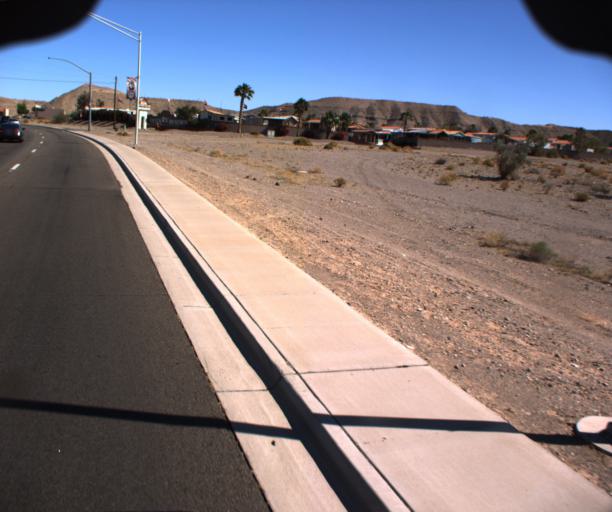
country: US
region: Arizona
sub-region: Mohave County
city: Bullhead City
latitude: 35.0687
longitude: -114.5891
